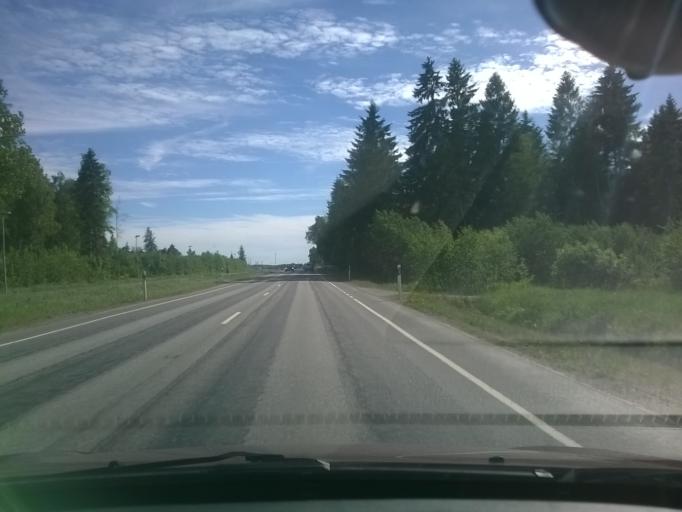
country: EE
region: Jaervamaa
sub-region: Paide linn
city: Paide
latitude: 58.9274
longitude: 25.6284
